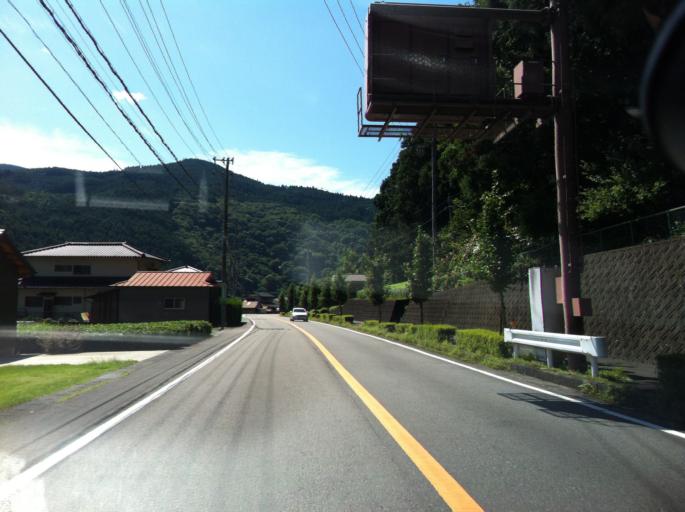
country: JP
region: Shizuoka
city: Fujieda
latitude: 35.0949
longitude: 138.1275
